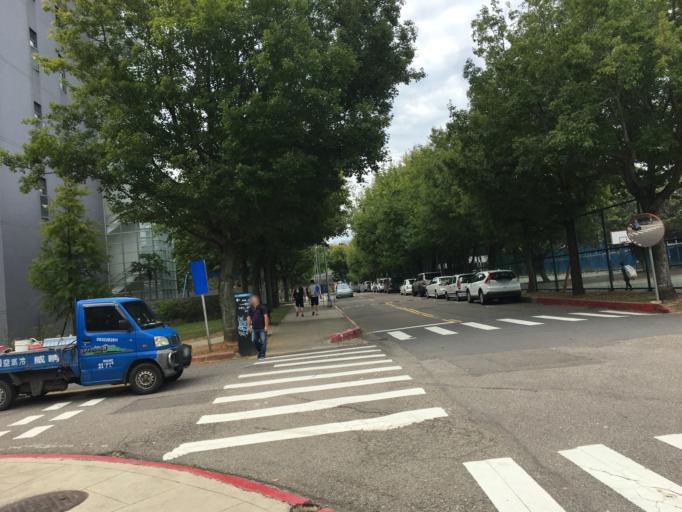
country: TW
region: Taiwan
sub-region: Hsinchu
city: Hsinchu
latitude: 24.7878
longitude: 120.9954
